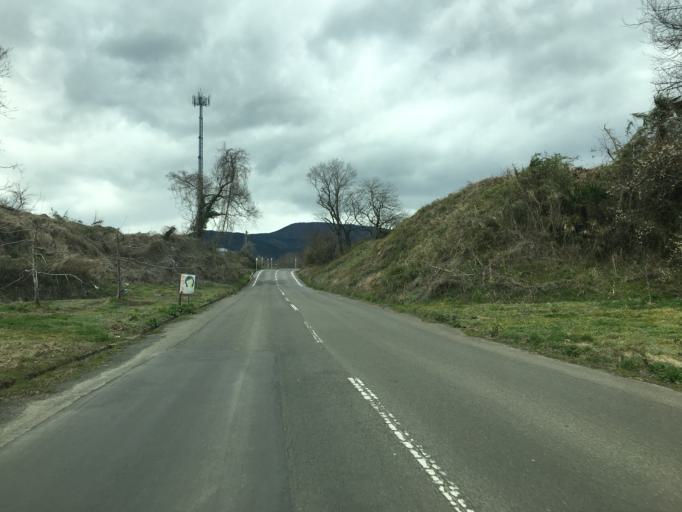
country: JP
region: Fukushima
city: Hobaramachi
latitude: 37.8496
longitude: 140.5343
